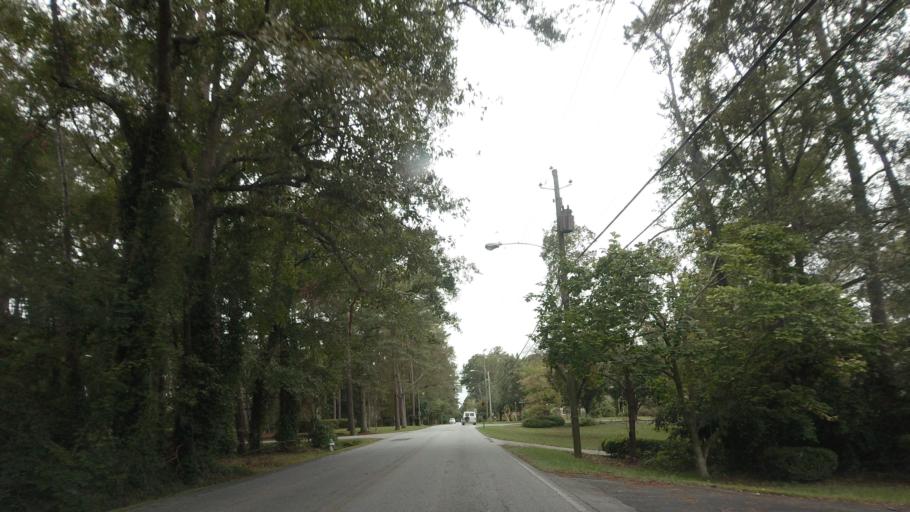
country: US
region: Georgia
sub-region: Lowndes County
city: Remerton
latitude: 30.8597
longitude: -83.2995
